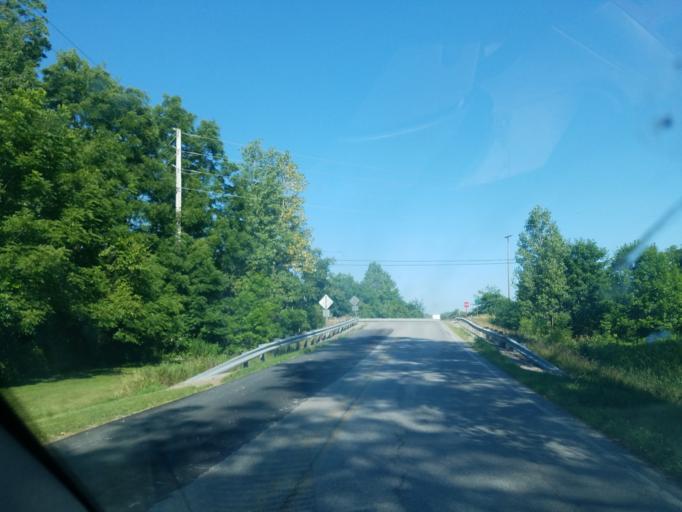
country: US
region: Ohio
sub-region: Union County
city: Richwood
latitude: 40.4146
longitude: -83.4521
